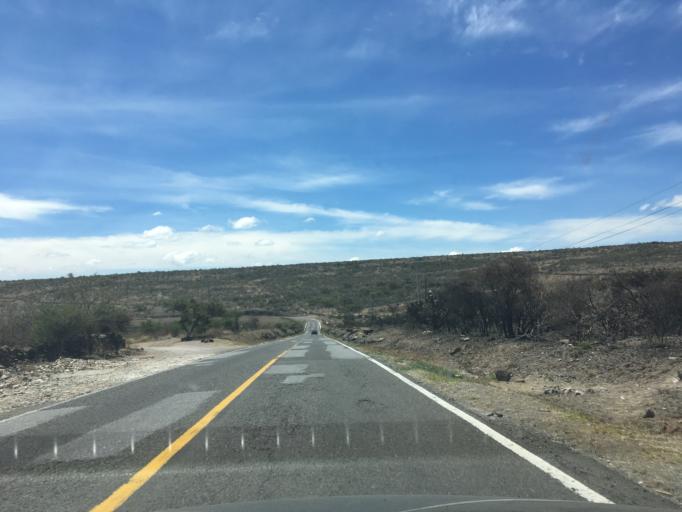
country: MX
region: Hidalgo
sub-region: Alfajayucan
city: Santa Maria Xigui
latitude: 20.4321
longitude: -99.4639
